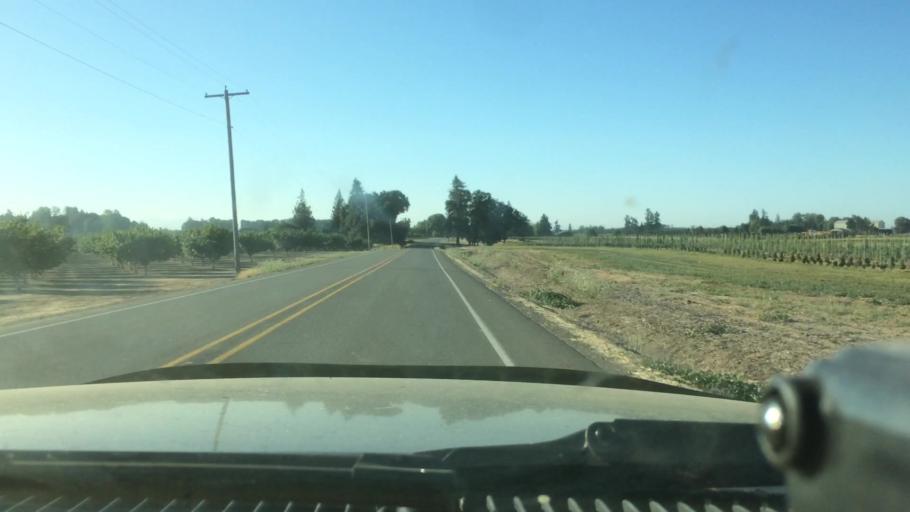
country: US
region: Oregon
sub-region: Marion County
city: Gervais
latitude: 45.1250
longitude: -122.9889
